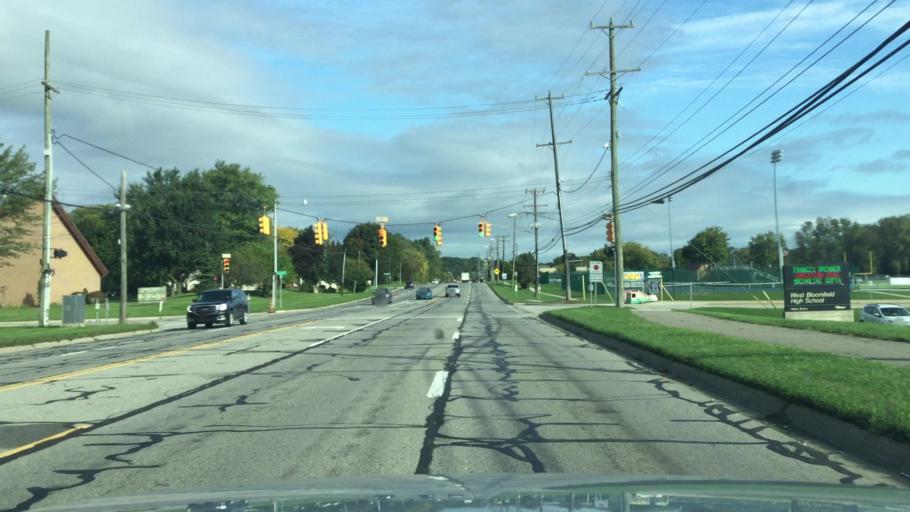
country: US
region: Michigan
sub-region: Oakland County
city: Orchard Lake
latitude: 42.5663
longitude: -83.3618
